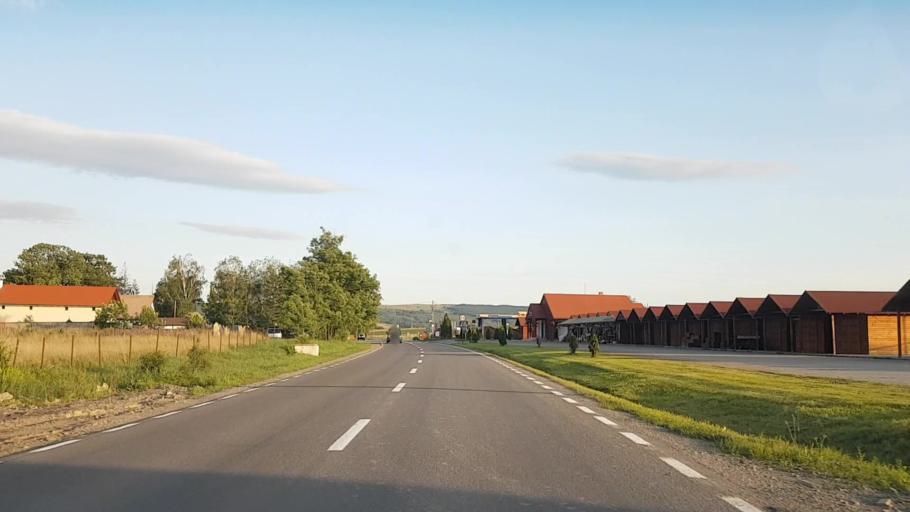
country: RO
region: Harghita
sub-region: Comuna Lupeni
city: Lupeni
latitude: 46.3779
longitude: 25.2194
